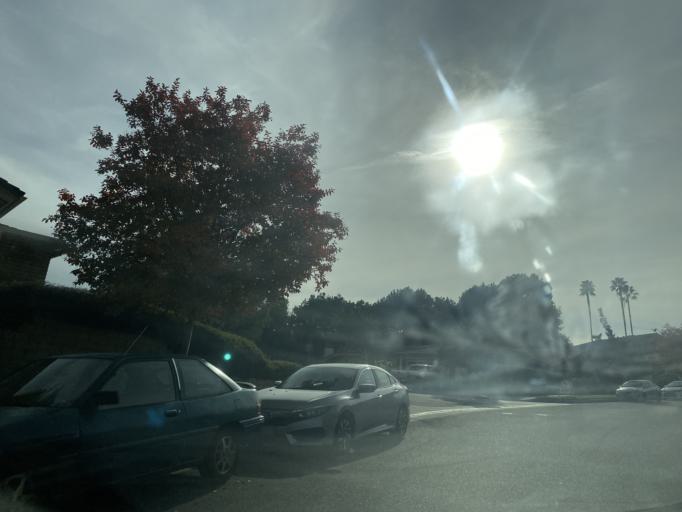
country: US
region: California
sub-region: Orange County
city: Brea
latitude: 33.8934
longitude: -117.8870
